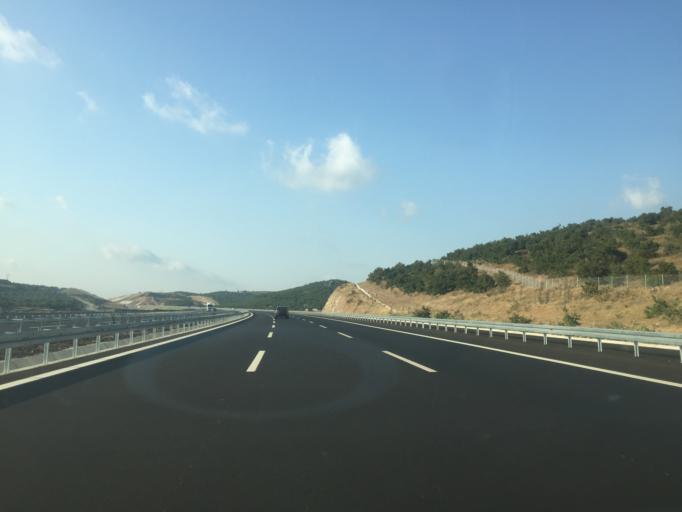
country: TR
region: Balikesir
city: Ertugrul
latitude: 39.5131
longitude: 27.6819
